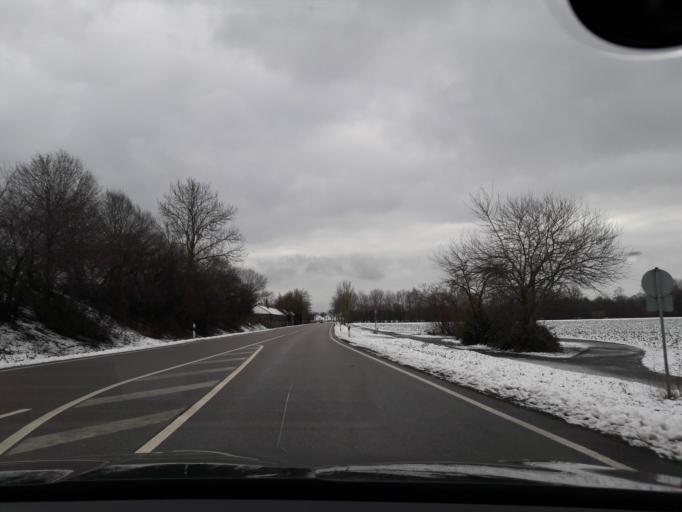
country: DE
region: Bavaria
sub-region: Upper Bavaria
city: Karlsfeld
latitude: 48.2440
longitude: 11.4762
